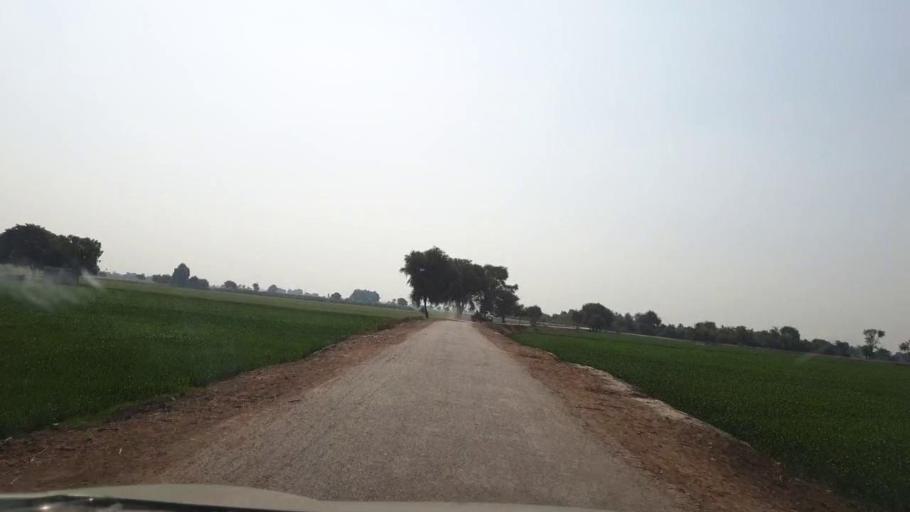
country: PK
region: Sindh
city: Bhit Shah
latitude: 25.7493
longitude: 68.4955
